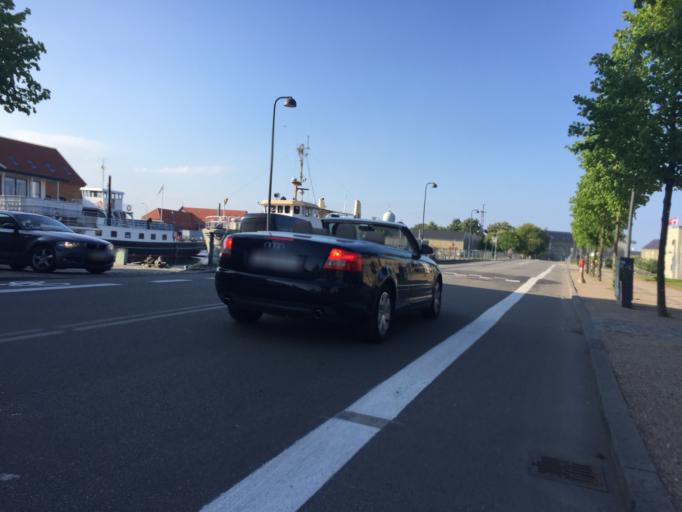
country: DK
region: Capital Region
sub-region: Kobenhavn
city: Christianshavn
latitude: 55.6825
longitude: 12.6057
